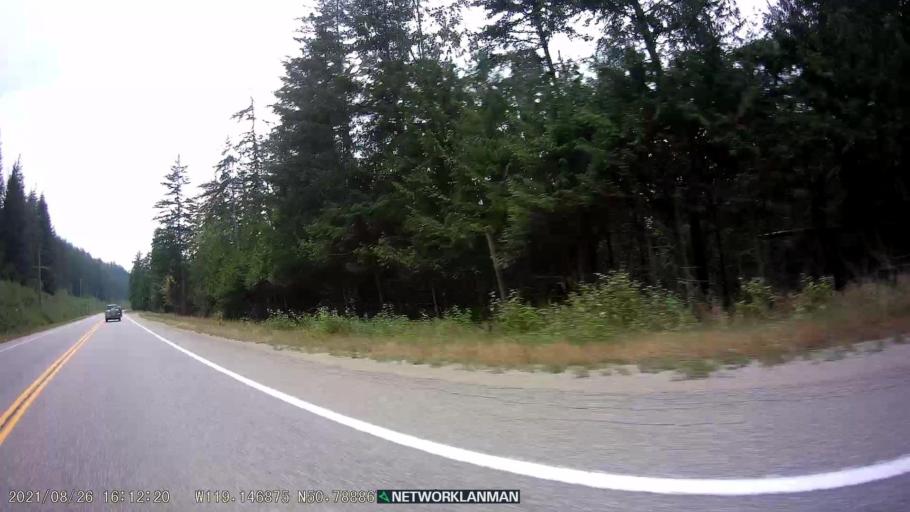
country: CA
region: British Columbia
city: Sicamous
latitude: 50.7890
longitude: -119.1475
